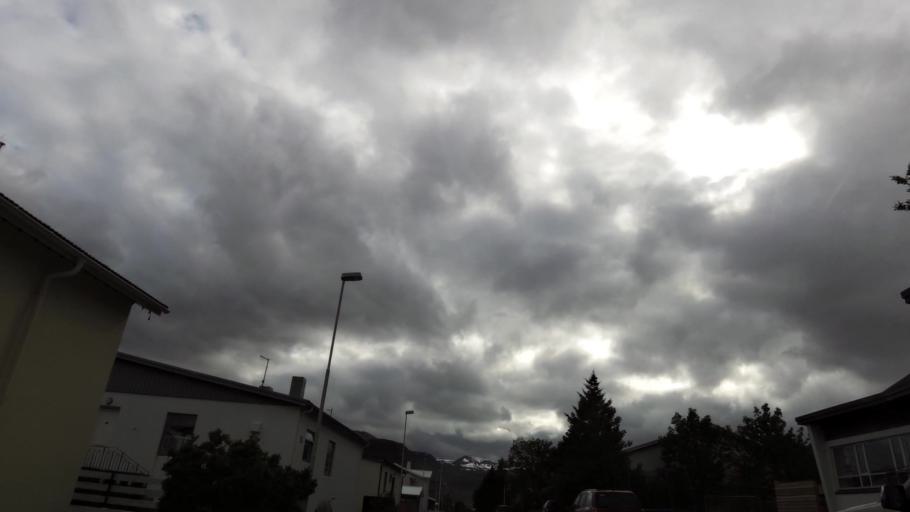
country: IS
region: Westfjords
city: Isafjoerdur
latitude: 66.0752
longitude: -23.1331
